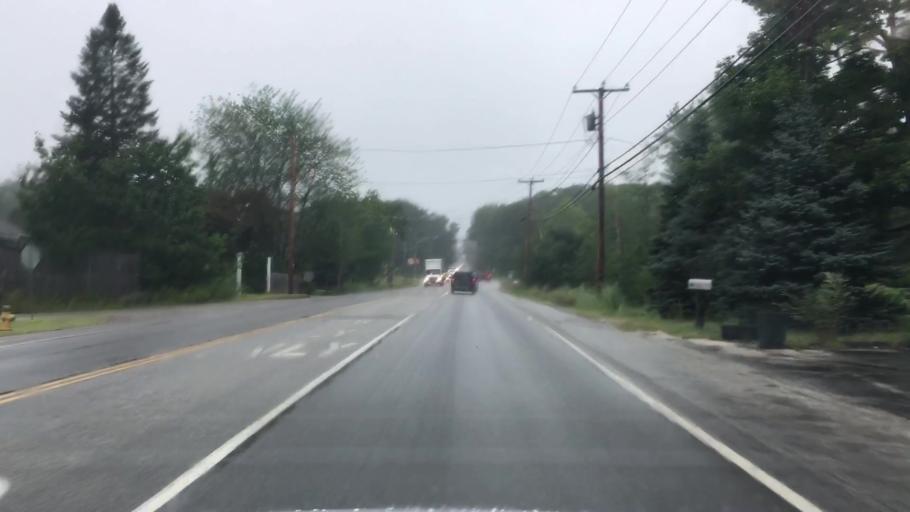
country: US
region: Maine
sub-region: Cumberland County
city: North Windham
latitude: 43.8102
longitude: -70.4181
